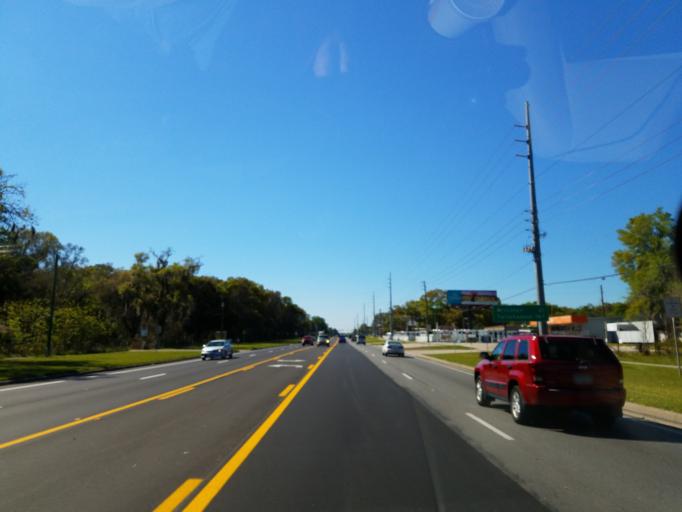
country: US
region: Florida
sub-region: Marion County
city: Ocala
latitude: 29.2087
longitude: -82.1893
